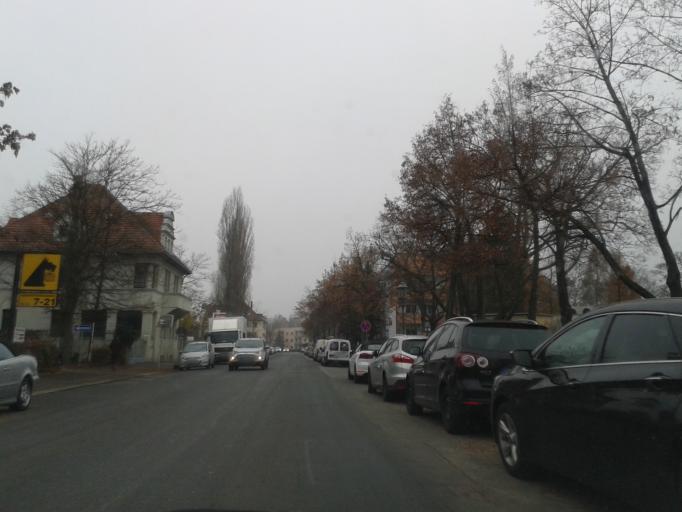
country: DE
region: Saxony
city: Dresden
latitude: 51.0899
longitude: 13.7084
